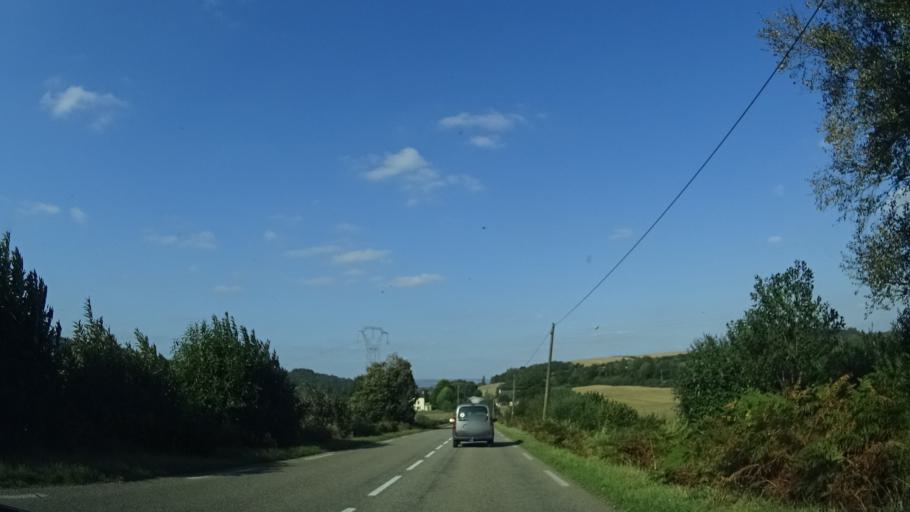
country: FR
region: Brittany
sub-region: Departement du Finistere
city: Chateaulin
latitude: 48.1818
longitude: -4.1110
